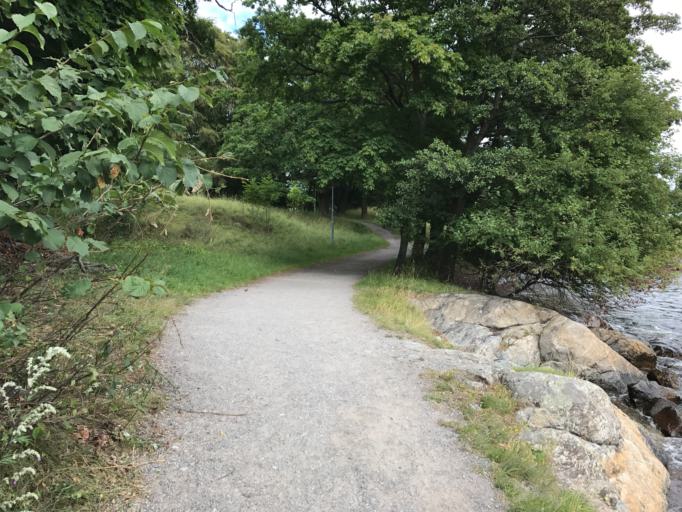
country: SE
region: Stockholm
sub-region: Stockholms Kommun
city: OEstermalm
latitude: 59.3203
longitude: 18.1210
